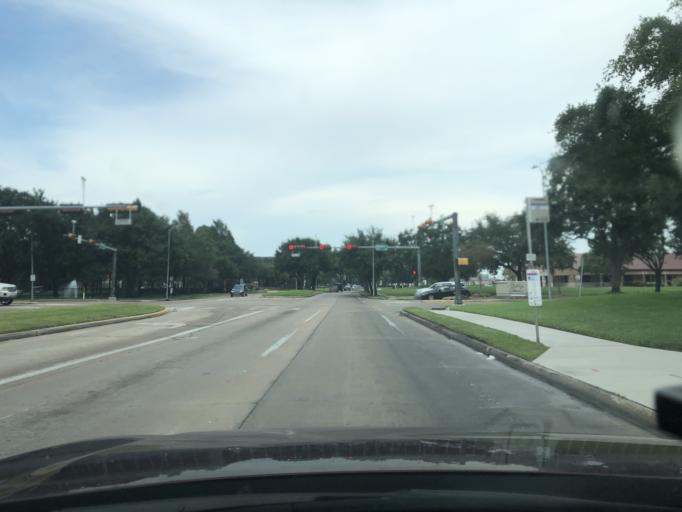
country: US
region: Texas
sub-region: Fort Bend County
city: Mission Bend
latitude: 29.7297
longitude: -95.6003
